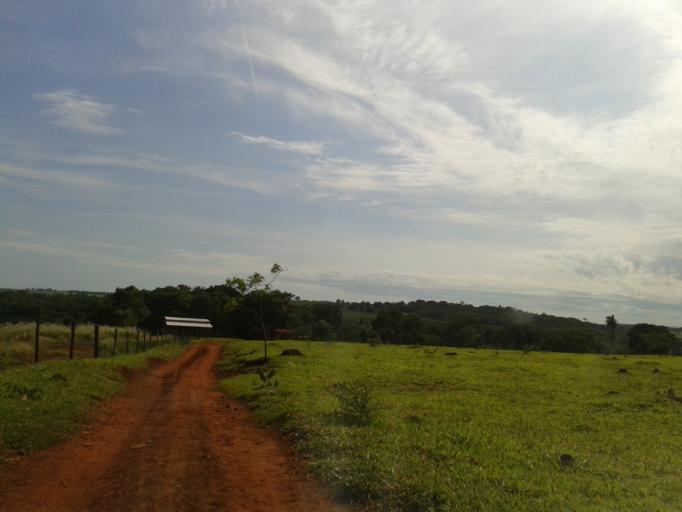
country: BR
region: Minas Gerais
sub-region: Centralina
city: Centralina
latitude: -18.7043
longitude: -49.2037
